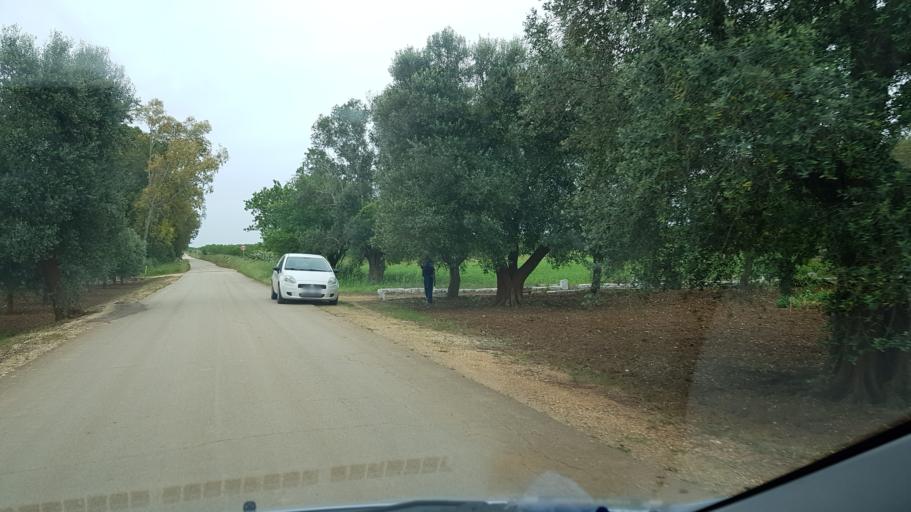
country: IT
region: Apulia
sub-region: Provincia di Brindisi
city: Mesagne
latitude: 40.6205
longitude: 17.7731
